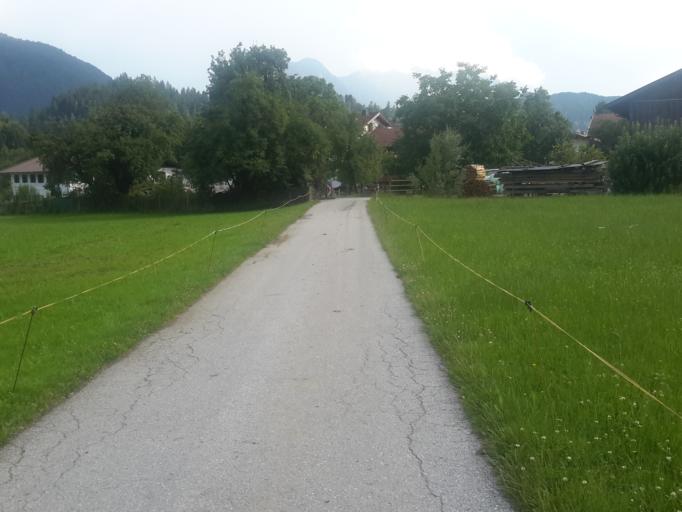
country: AT
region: Tyrol
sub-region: Politischer Bezirk Kufstein
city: Kufstein
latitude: 47.5888
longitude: 12.1544
